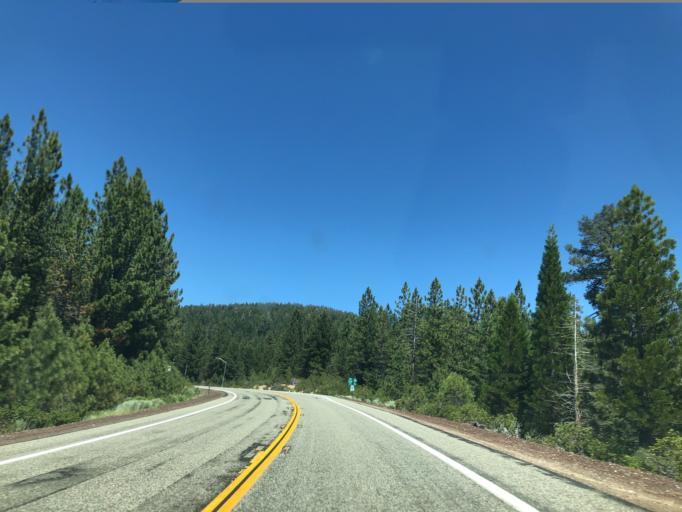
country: US
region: California
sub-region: Shasta County
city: Shingletown
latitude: 40.5426
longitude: -121.5795
